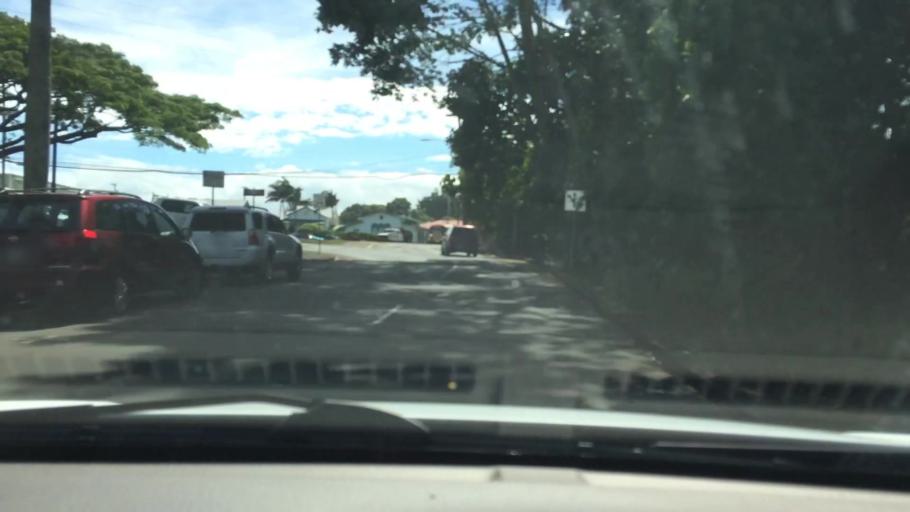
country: US
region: Hawaii
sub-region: Hawaii County
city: Hilo
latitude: 19.7265
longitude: -155.0892
